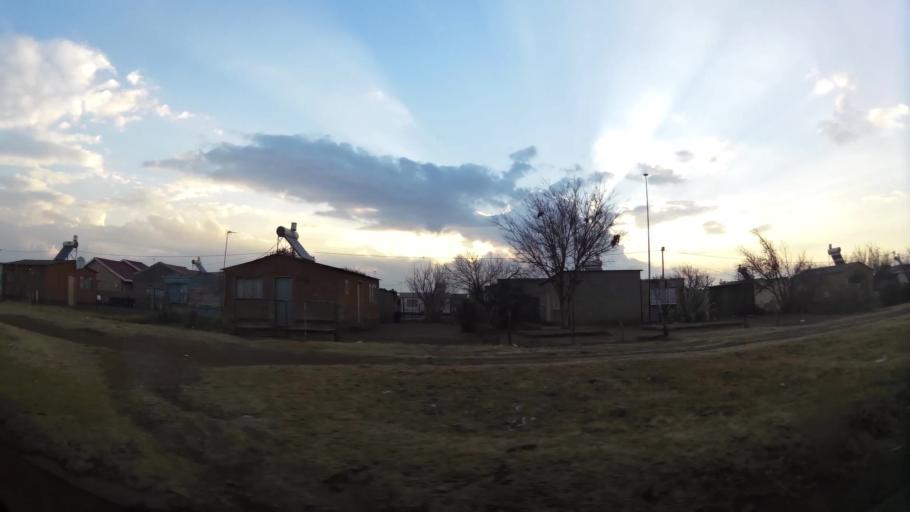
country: ZA
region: Gauteng
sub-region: City of Johannesburg Metropolitan Municipality
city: Orange Farm
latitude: -26.5585
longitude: 27.8385
